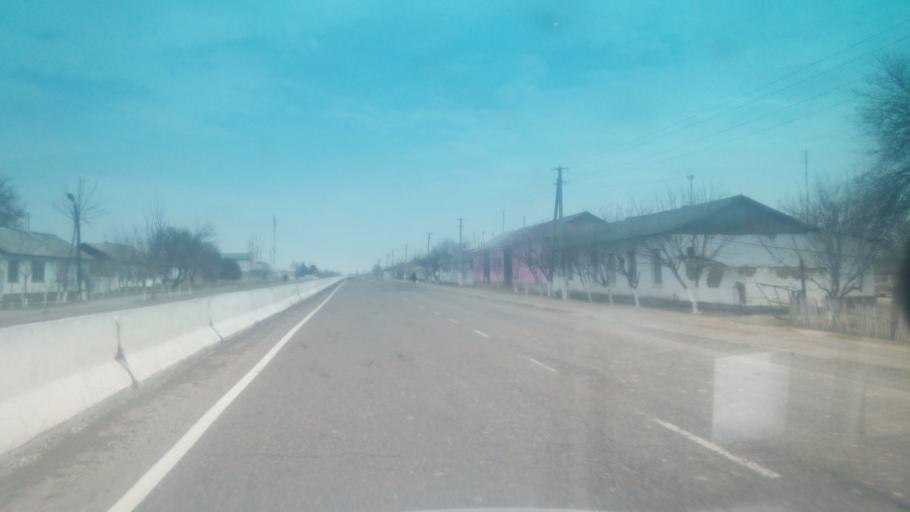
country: KZ
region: Ongtustik Qazaqstan
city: Myrzakent
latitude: 40.4997
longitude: 68.5696
